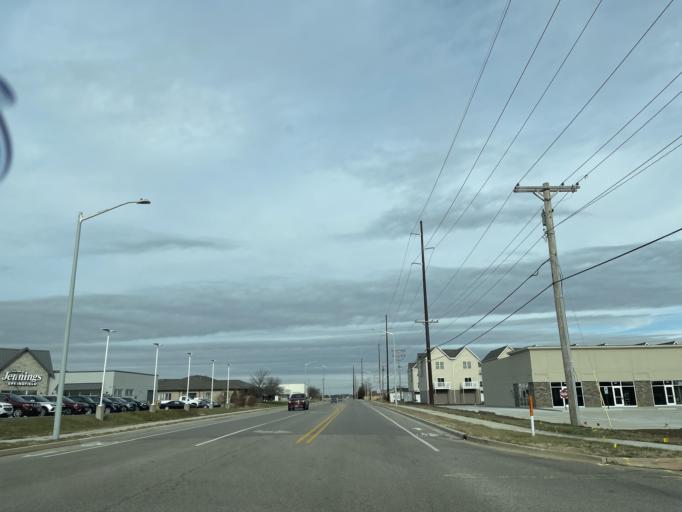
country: US
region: Illinois
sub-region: Sangamon County
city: Jerome
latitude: 39.7574
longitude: -89.7343
